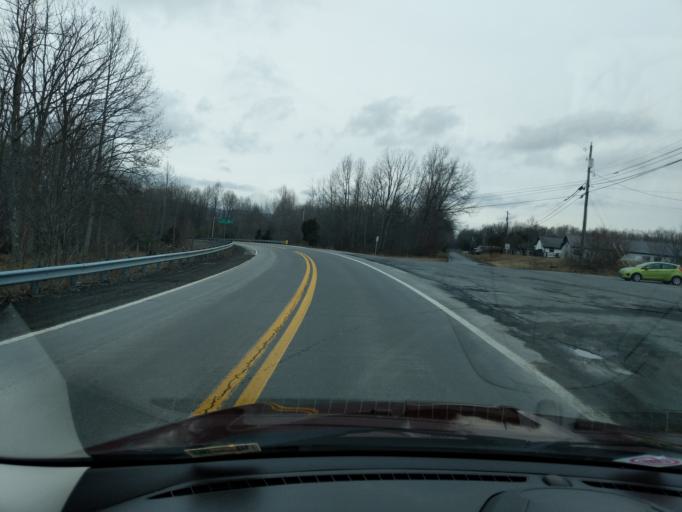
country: US
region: West Virginia
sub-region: Greenbrier County
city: Lewisburg
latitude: 37.8566
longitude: -80.5499
